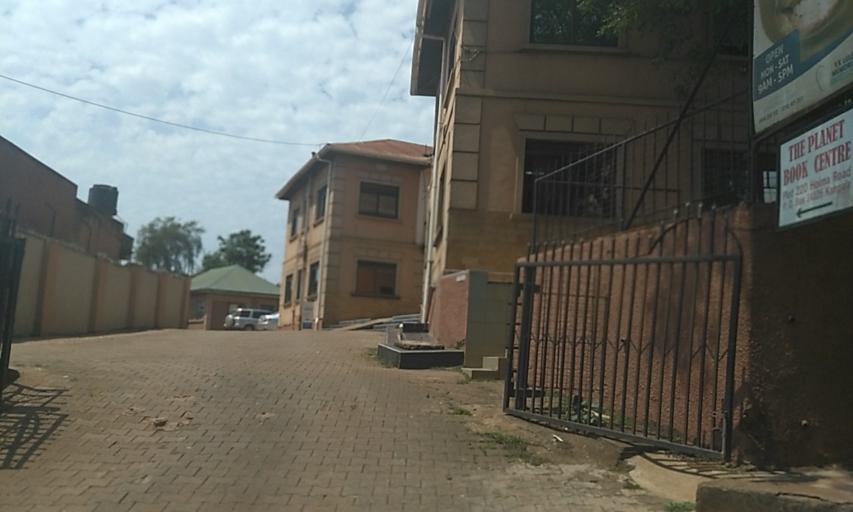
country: UG
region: Central Region
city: Kampala Central Division
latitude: 0.3124
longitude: 32.5656
